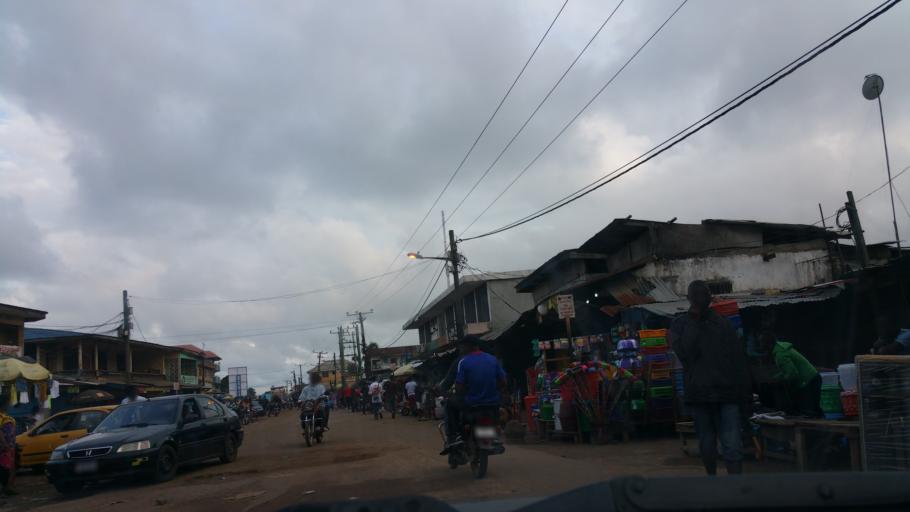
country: LR
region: Montserrado
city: Monrovia
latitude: 6.2802
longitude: -10.7506
